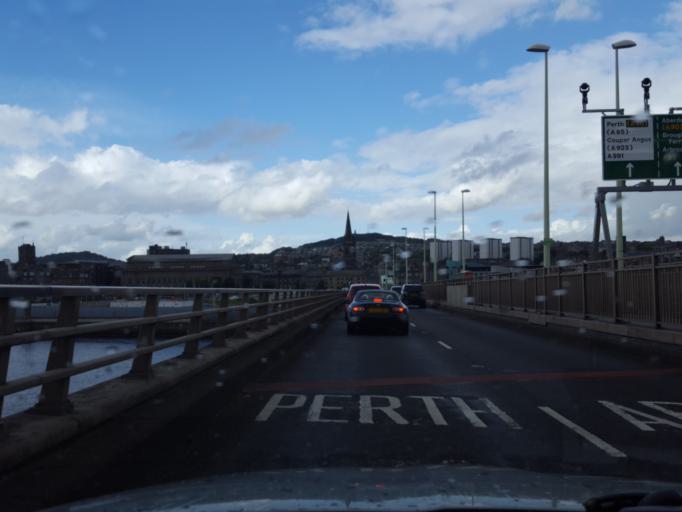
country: GB
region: Scotland
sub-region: Dundee City
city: Dundee
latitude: 56.4579
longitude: -2.9604
